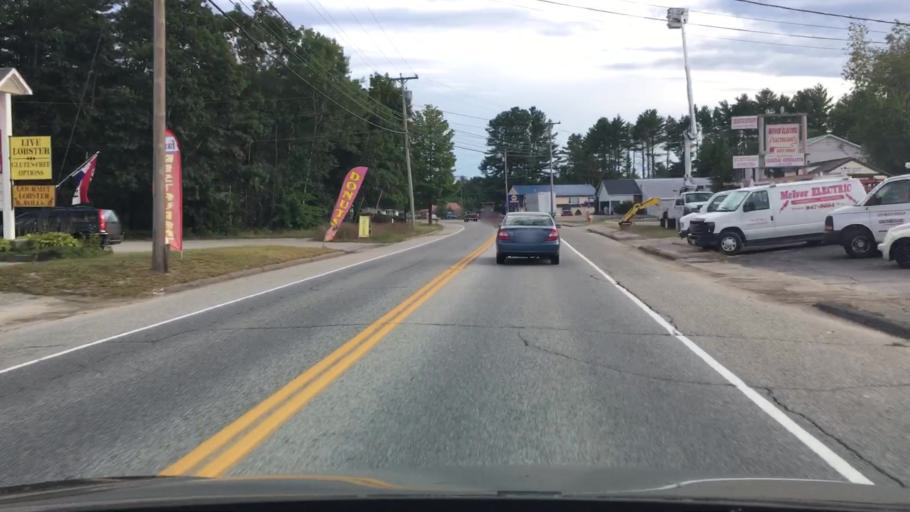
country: US
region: Maine
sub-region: Cumberland County
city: Bridgton
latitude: 44.0390
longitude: -70.6999
